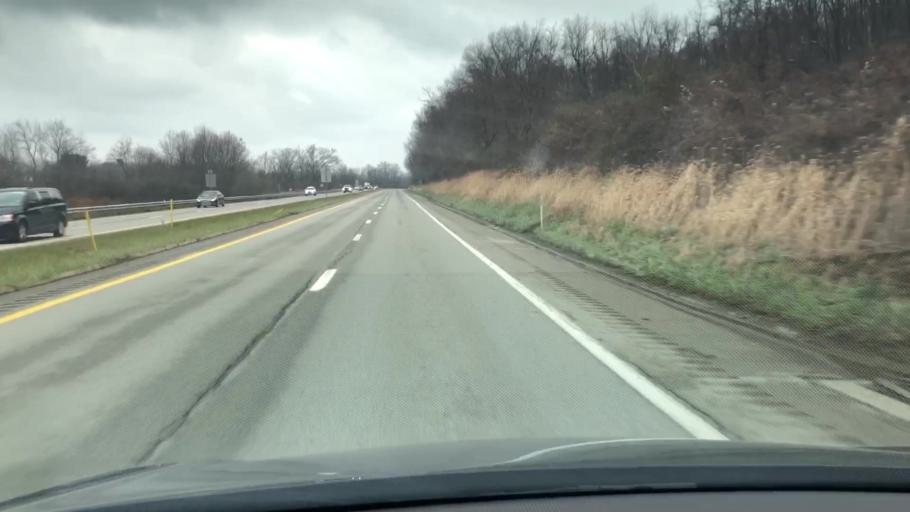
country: US
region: Pennsylvania
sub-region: Westmoreland County
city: Scottdale
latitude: 40.0803
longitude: -79.5618
